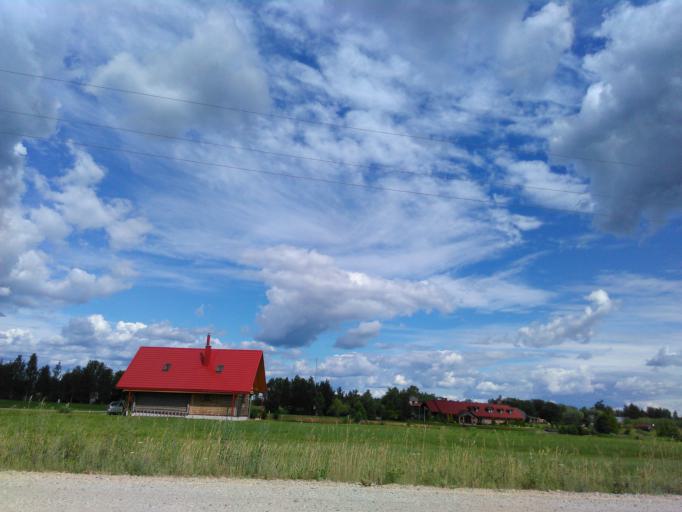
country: LV
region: Beverina
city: Murmuiza
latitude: 57.4697
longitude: 25.4871
